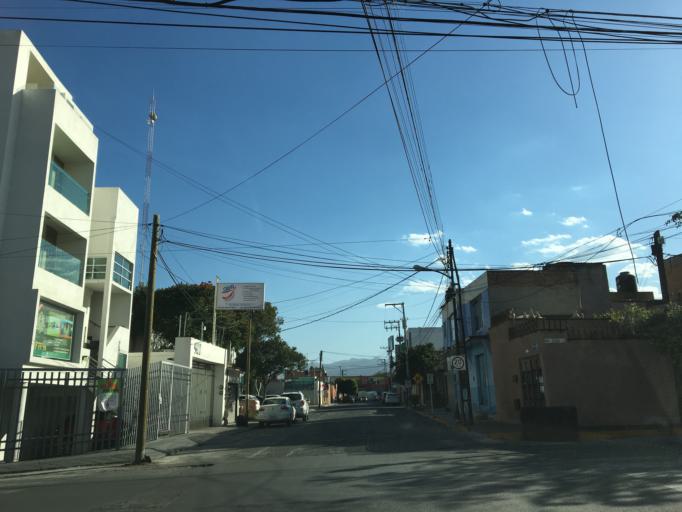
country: MX
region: San Luis Potosi
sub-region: San Luis Potosi
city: San Luis Potosi
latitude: 22.1461
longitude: -100.9925
